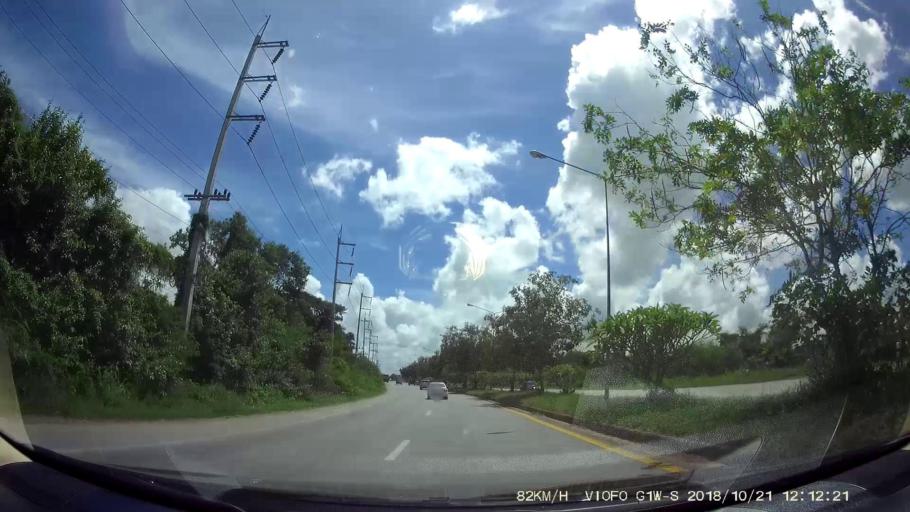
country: TH
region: Chaiyaphum
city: Chatturat
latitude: 15.4080
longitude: 101.8346
